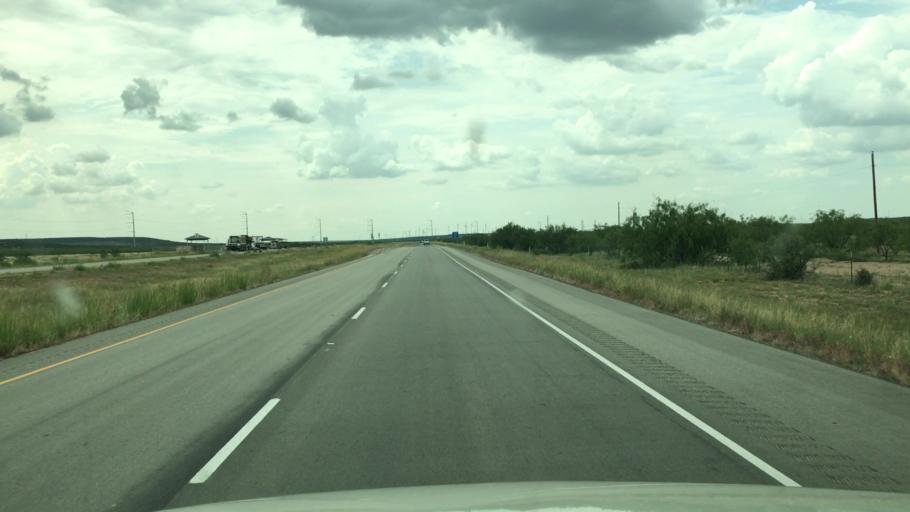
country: US
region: Texas
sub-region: Sterling County
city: Sterling City
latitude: 31.9649
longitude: -101.2265
